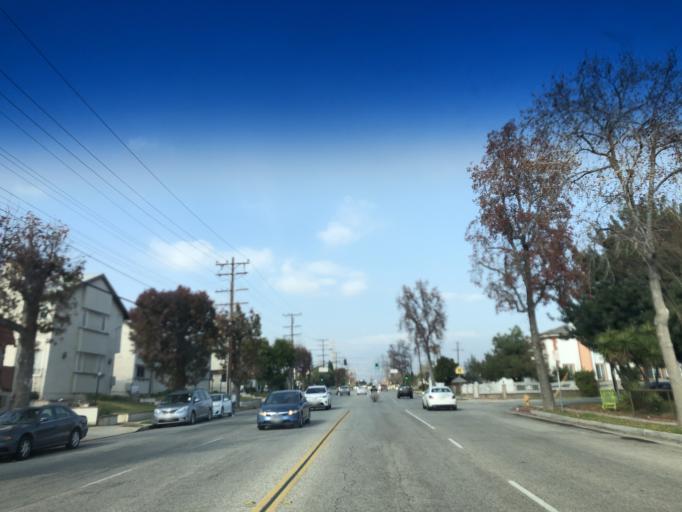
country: US
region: California
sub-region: Los Angeles County
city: Rosemead
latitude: 34.0833
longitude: -118.0821
